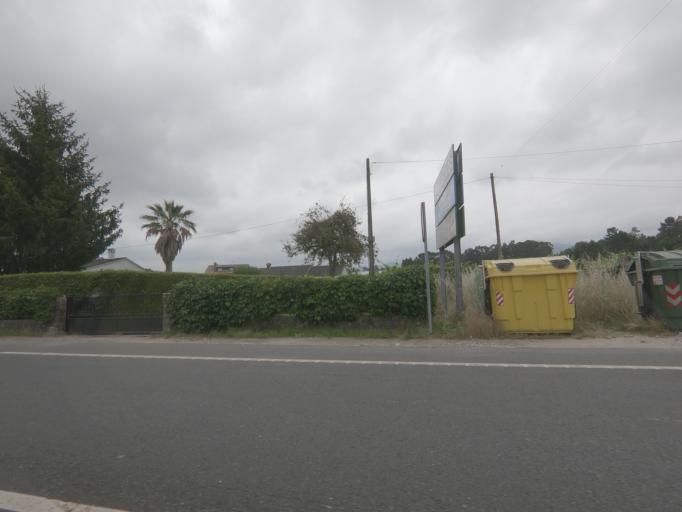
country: ES
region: Galicia
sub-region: Provincia de Pontevedra
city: Tomino
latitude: 41.9921
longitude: -8.7069
